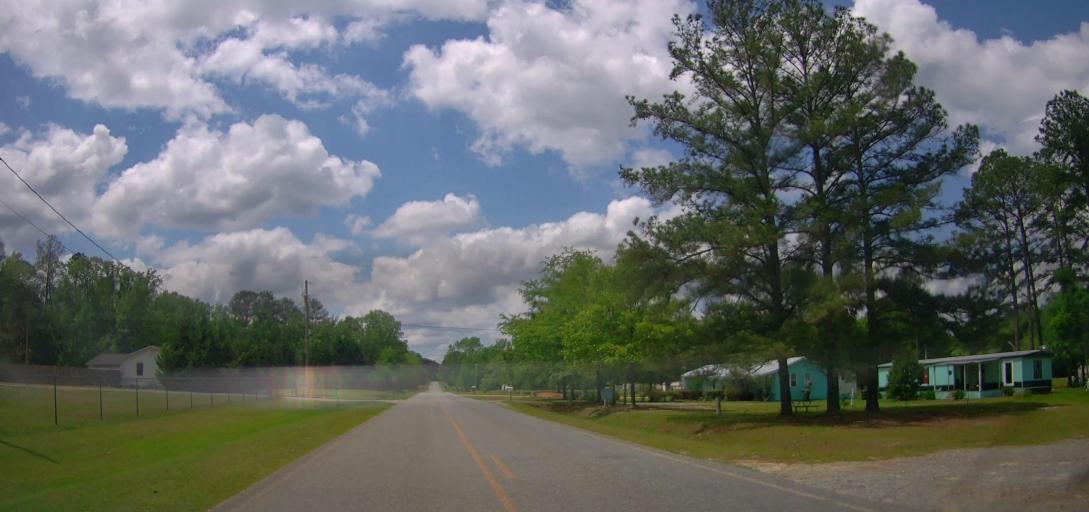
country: US
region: Georgia
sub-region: Laurens County
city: Dublin
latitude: 32.5972
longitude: -83.0156
